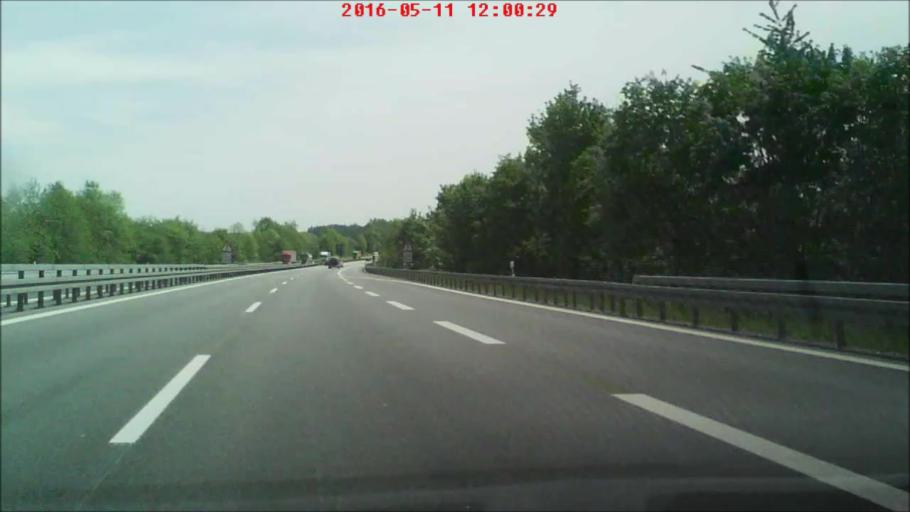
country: DE
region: Bavaria
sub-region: Lower Bavaria
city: Windberg
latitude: 48.9204
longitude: 12.7337
